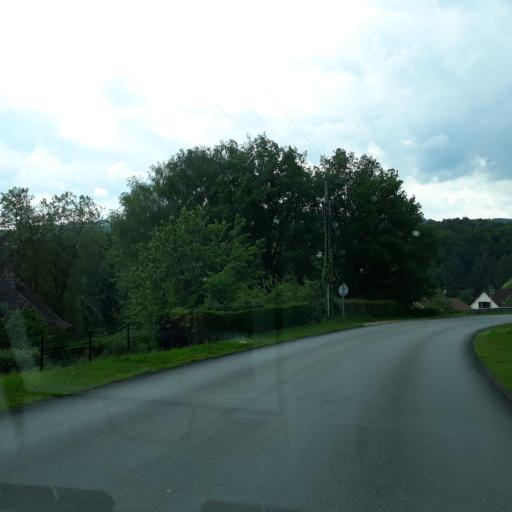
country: FR
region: Limousin
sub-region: Departement de la Haute-Vienne
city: Eymoutiers
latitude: 45.7467
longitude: 1.7410
